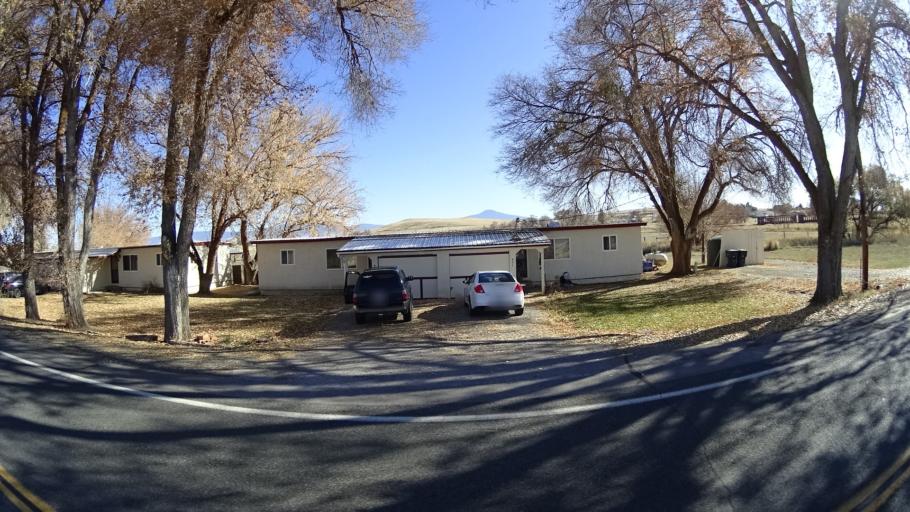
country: US
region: California
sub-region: Siskiyou County
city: Montague
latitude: 41.7358
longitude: -122.5246
